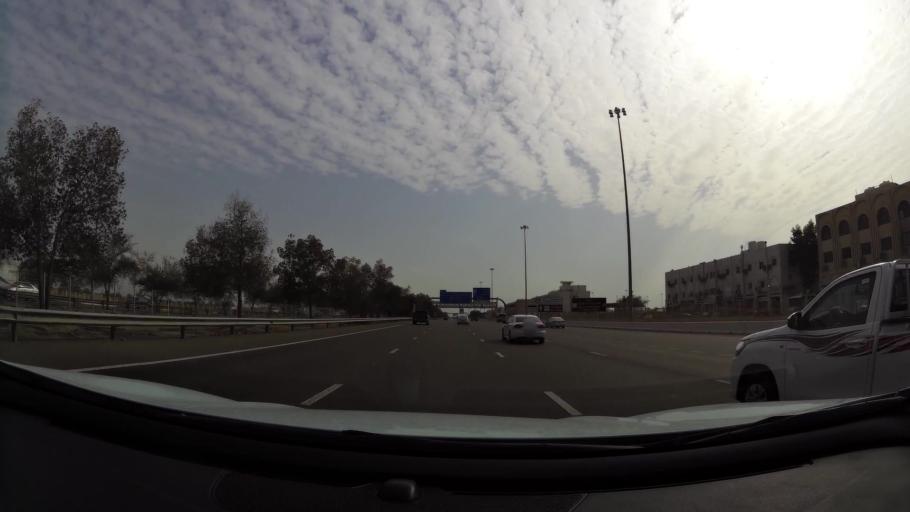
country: AE
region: Abu Dhabi
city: Abu Dhabi
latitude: 24.5581
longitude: 54.6950
